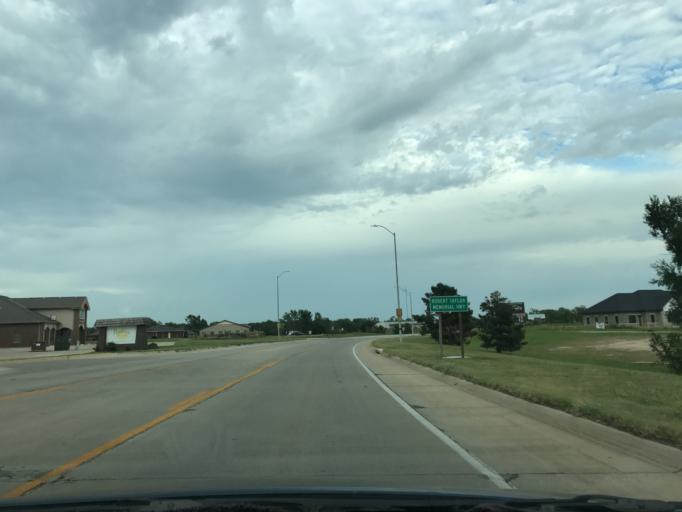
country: US
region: Nebraska
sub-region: Gage County
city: Beatrice
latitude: 40.2657
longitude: -96.7201
